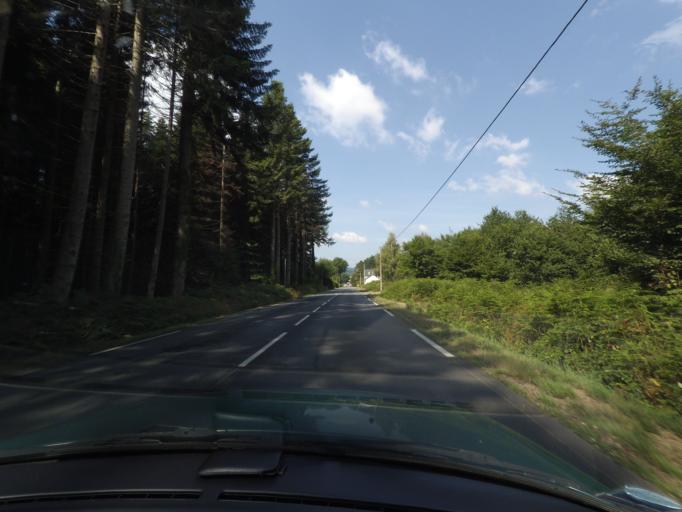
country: FR
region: Limousin
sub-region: Departement de la Haute-Vienne
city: Neuvic-Entier
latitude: 45.7607
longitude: 1.5811
